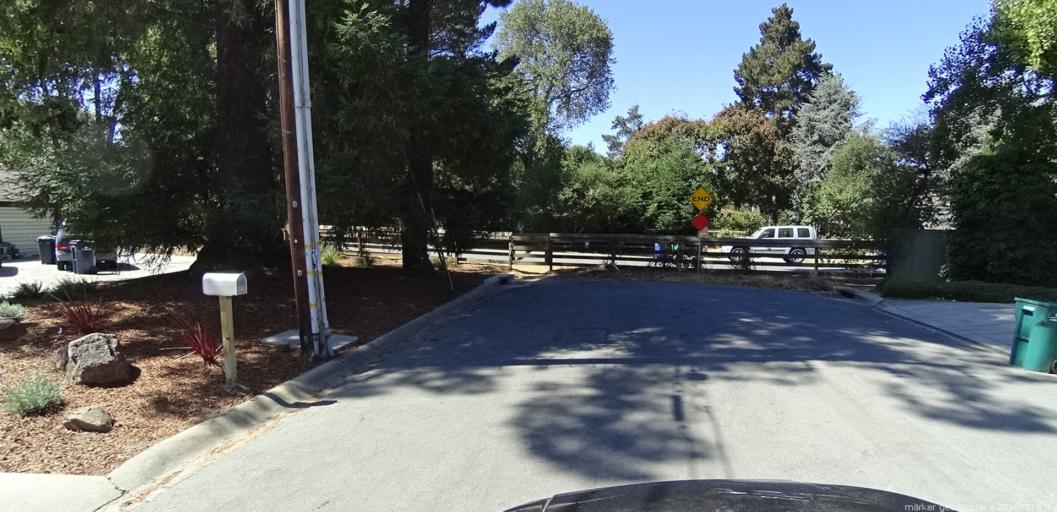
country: US
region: California
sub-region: Monterey County
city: Carmel-by-the-Sea
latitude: 36.5376
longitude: -121.8700
